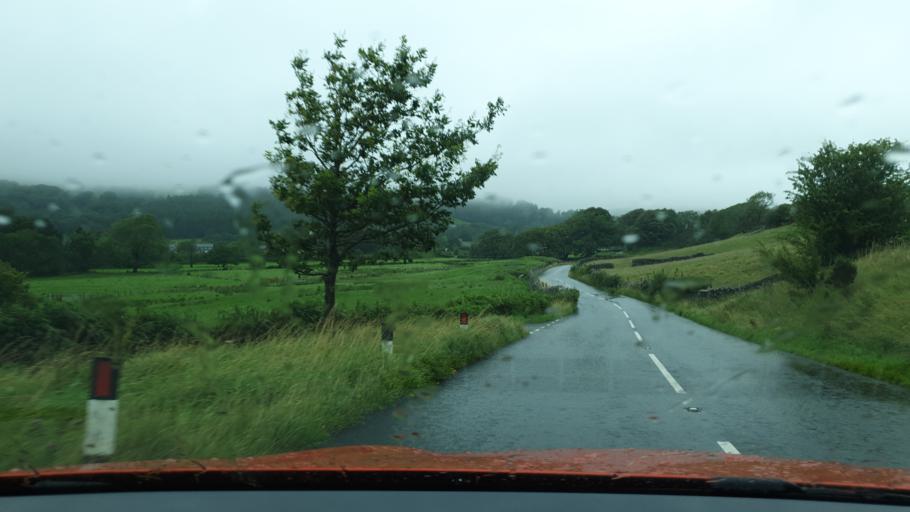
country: GB
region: England
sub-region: Cumbria
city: Ulverston
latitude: 54.3332
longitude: -3.0983
